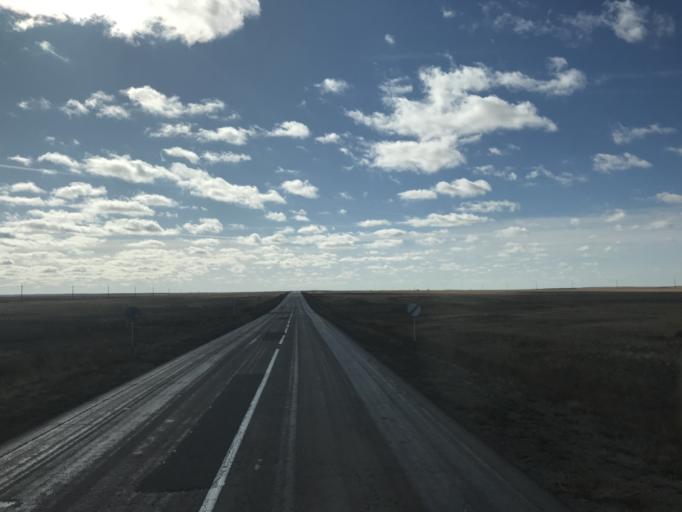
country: RU
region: Orenburg
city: Yasnyy
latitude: 50.4680
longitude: 60.1615
